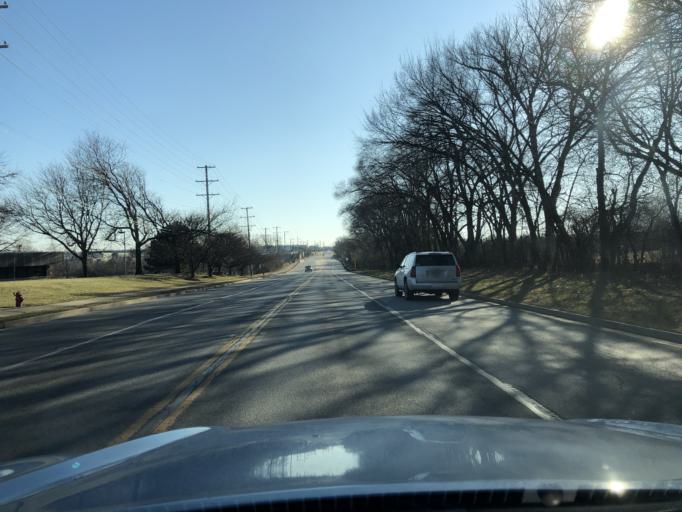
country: US
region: Illinois
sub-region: DuPage County
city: Itasca
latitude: 41.9750
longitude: -87.9983
